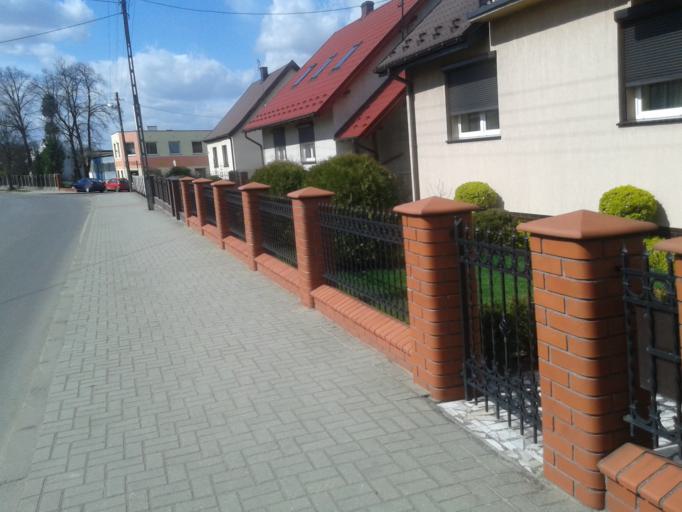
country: PL
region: Lower Silesian Voivodeship
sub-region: Powiat olesnicki
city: Miedzyborz
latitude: 51.3983
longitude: 17.6607
